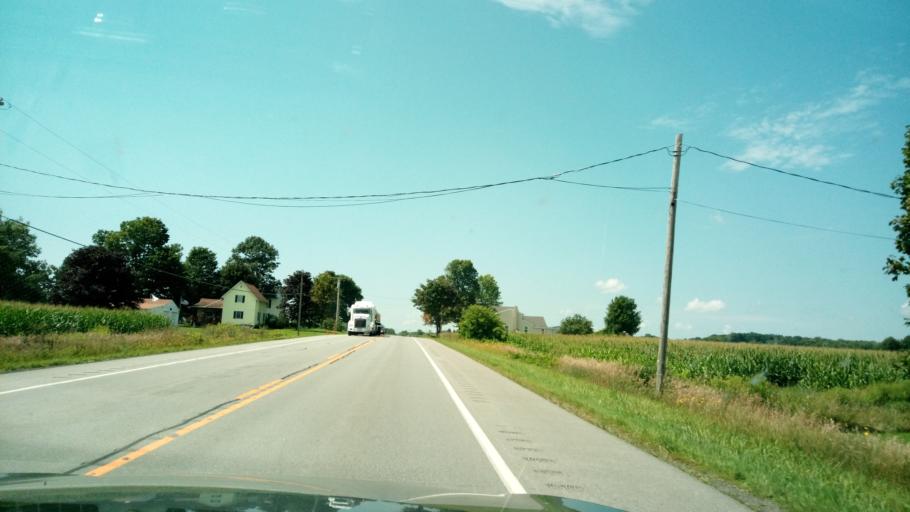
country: US
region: New York
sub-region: Wyoming County
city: Perry
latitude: 42.8327
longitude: -77.9500
